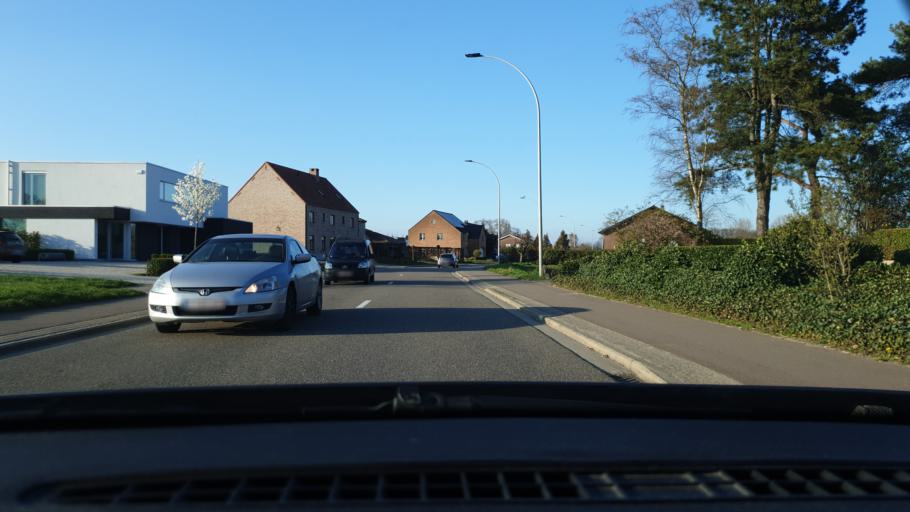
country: BE
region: Flanders
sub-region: Provincie Antwerpen
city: Geel
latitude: 51.1417
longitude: 4.9808
